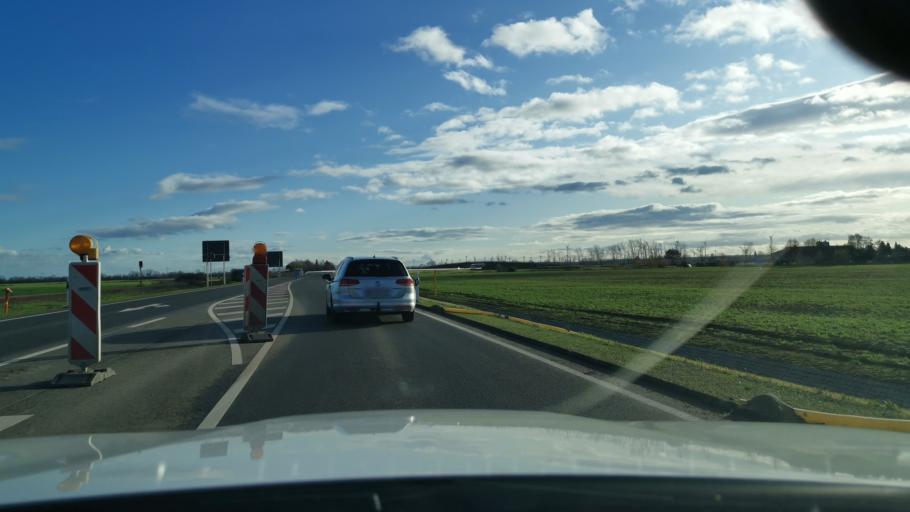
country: DE
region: Saxony-Anhalt
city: Wittenburg
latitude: 51.8256
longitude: 12.6409
